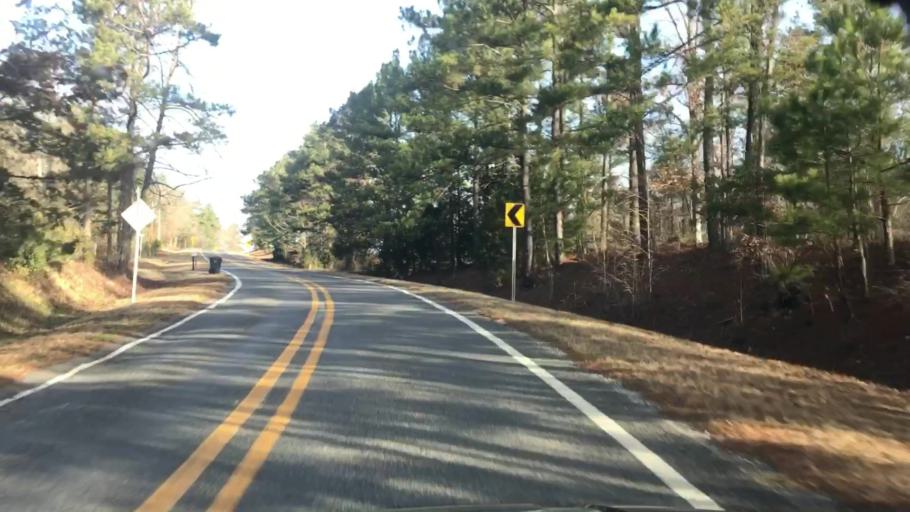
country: US
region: Arkansas
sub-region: Garland County
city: Rockwell
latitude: 34.4926
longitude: -93.2757
